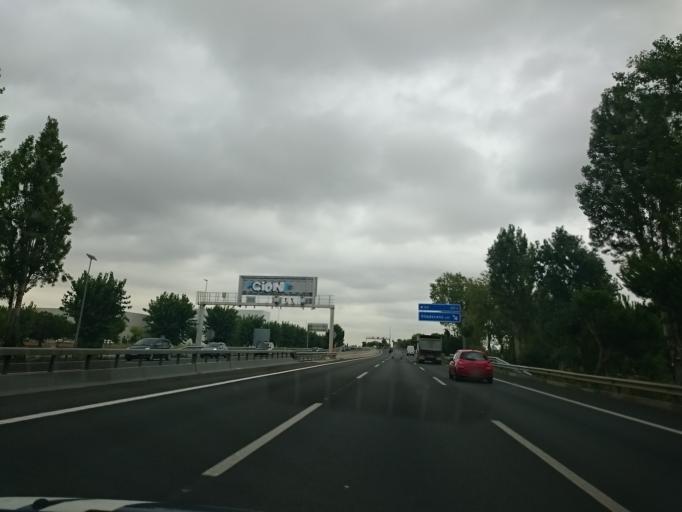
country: ES
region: Catalonia
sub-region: Provincia de Barcelona
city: Viladecans
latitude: 41.2972
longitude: 2.0175
